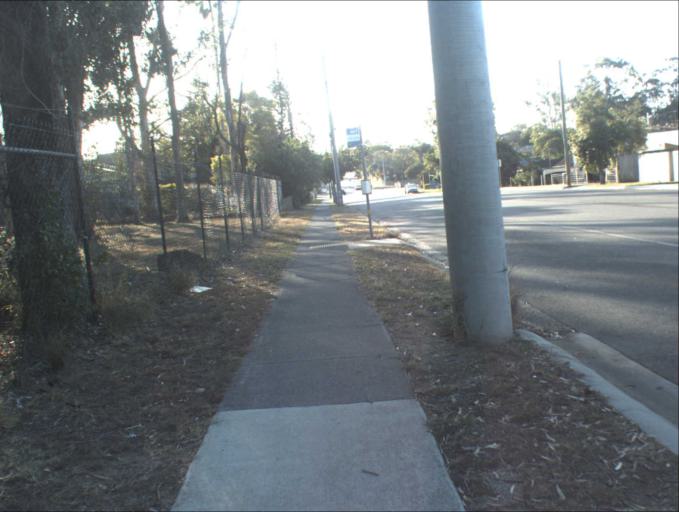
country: AU
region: Queensland
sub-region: Gold Coast
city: Yatala
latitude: -27.7103
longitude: 153.2138
